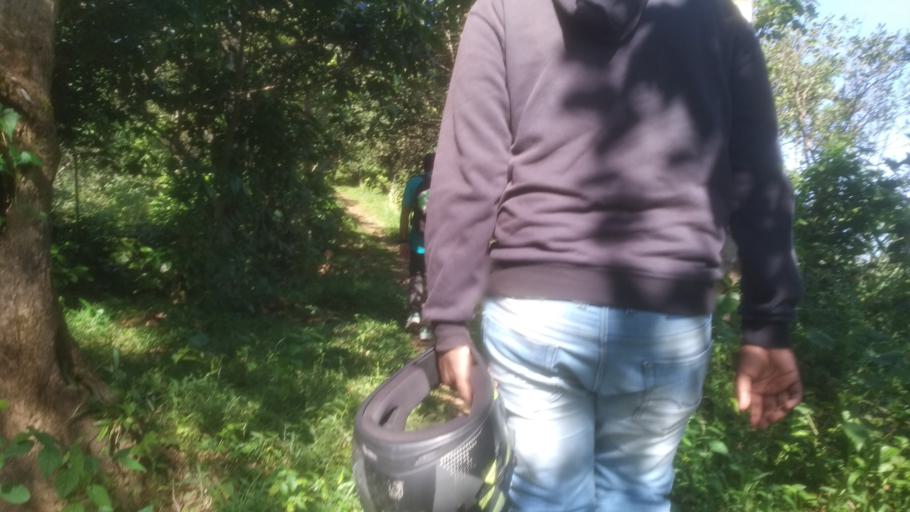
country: IN
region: Kerala
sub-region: Idukki
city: Idukki
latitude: 9.9805
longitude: 76.8322
